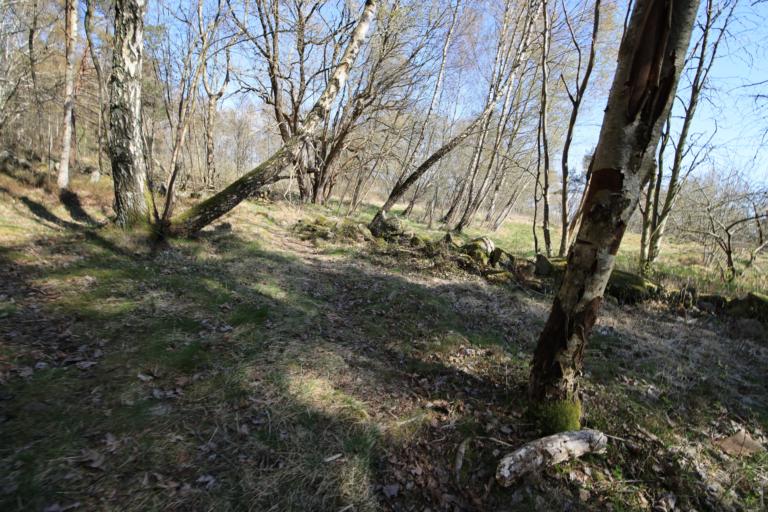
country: SE
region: Halland
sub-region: Varbergs Kommun
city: Traslovslage
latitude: 57.0563
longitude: 12.2853
